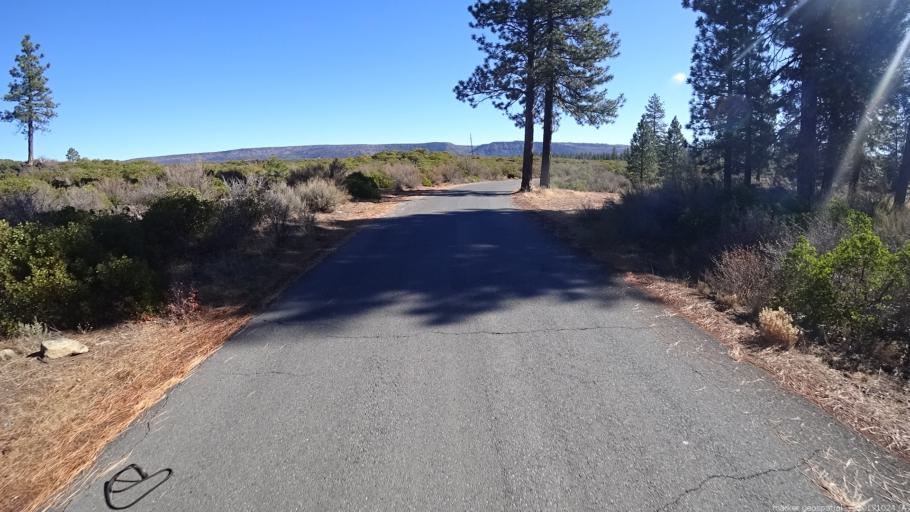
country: US
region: California
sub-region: Shasta County
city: Burney
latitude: 40.7511
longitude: -121.4742
